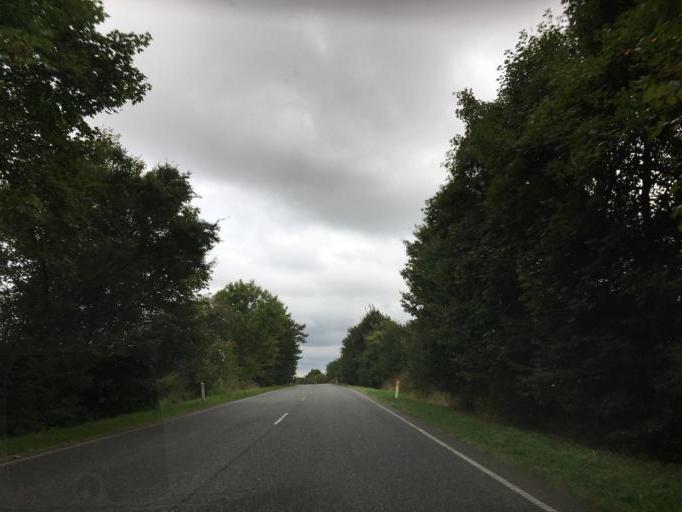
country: DK
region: South Denmark
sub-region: Kolding Kommune
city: Kolding
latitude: 55.5756
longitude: 9.4995
